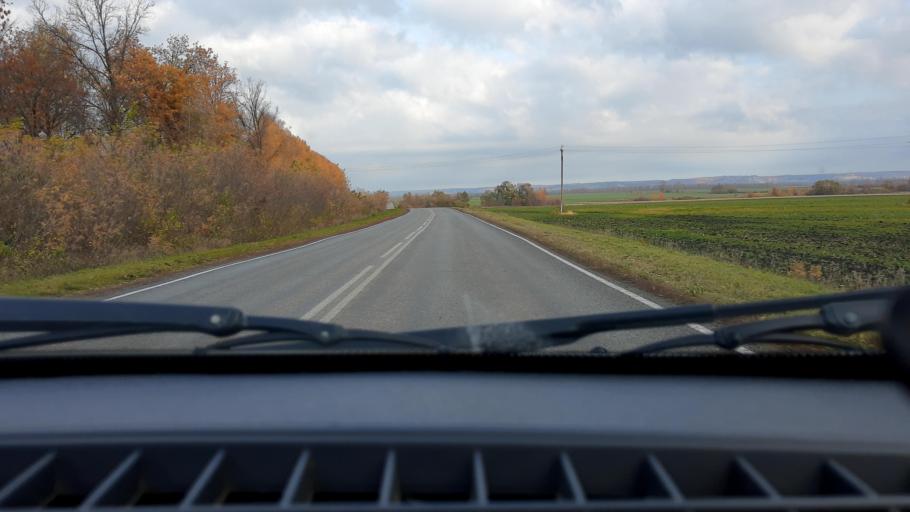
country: RU
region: Bashkortostan
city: Ulukulevo
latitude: 54.3965
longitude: 56.3795
